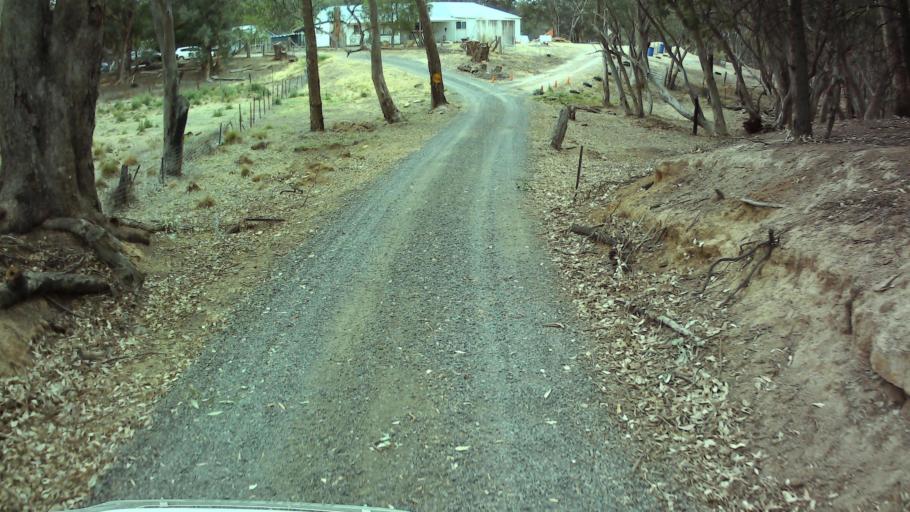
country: AU
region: New South Wales
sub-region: Cowra
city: Cowra
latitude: -33.9091
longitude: 148.4369
